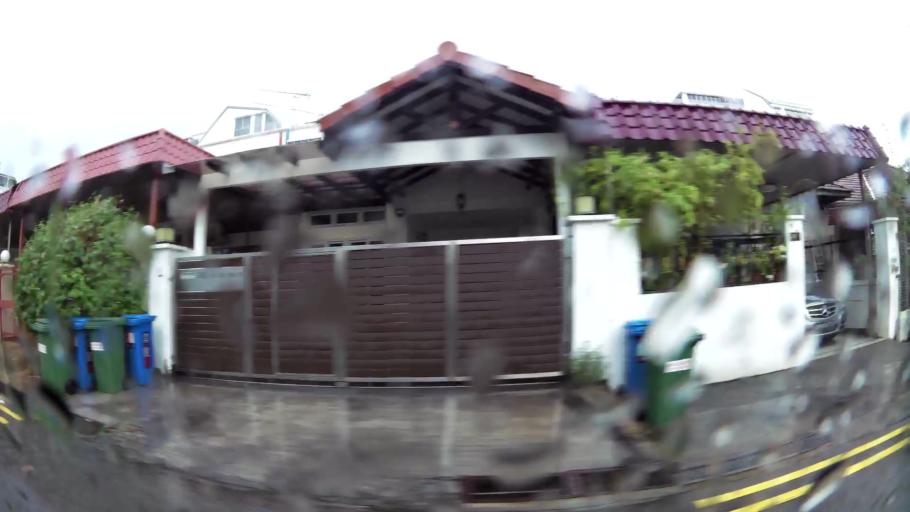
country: SG
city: Singapore
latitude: 1.3542
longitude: 103.8767
